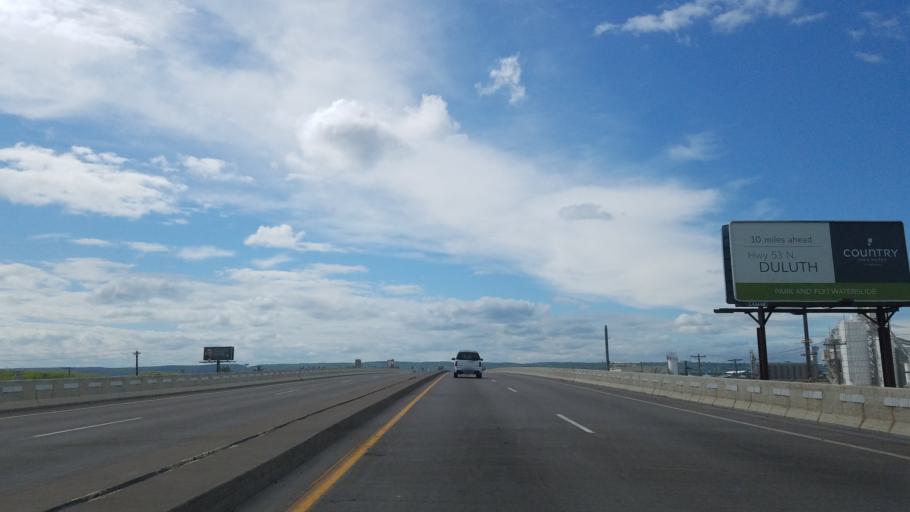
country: US
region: Wisconsin
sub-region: Douglas County
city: Superior
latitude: 46.7271
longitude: -92.0757
